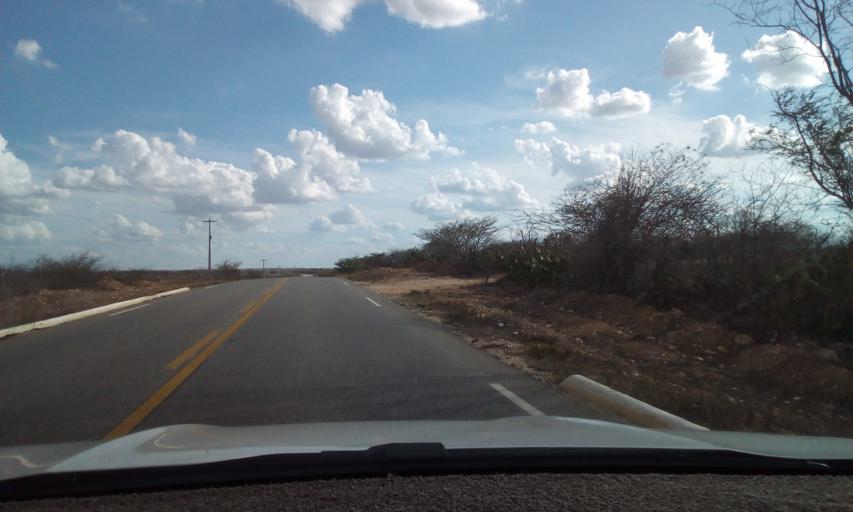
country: BR
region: Paraiba
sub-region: Soledade
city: Soledade
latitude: -6.8103
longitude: -36.4039
